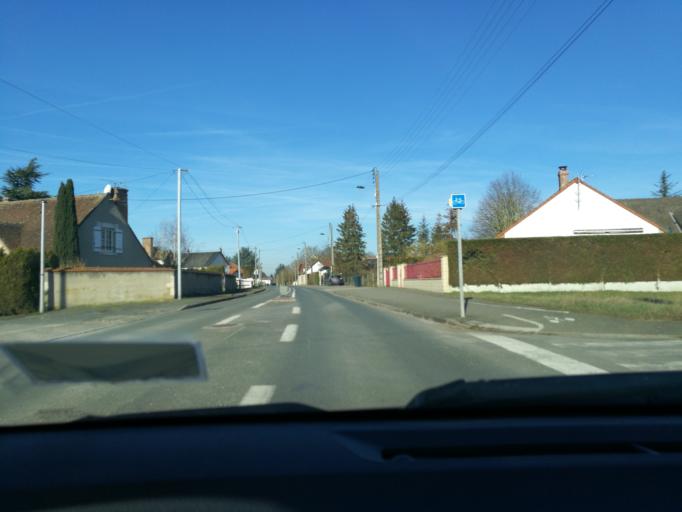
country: FR
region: Centre
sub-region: Departement du Loiret
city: Chaingy
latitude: 47.8792
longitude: 1.7809
